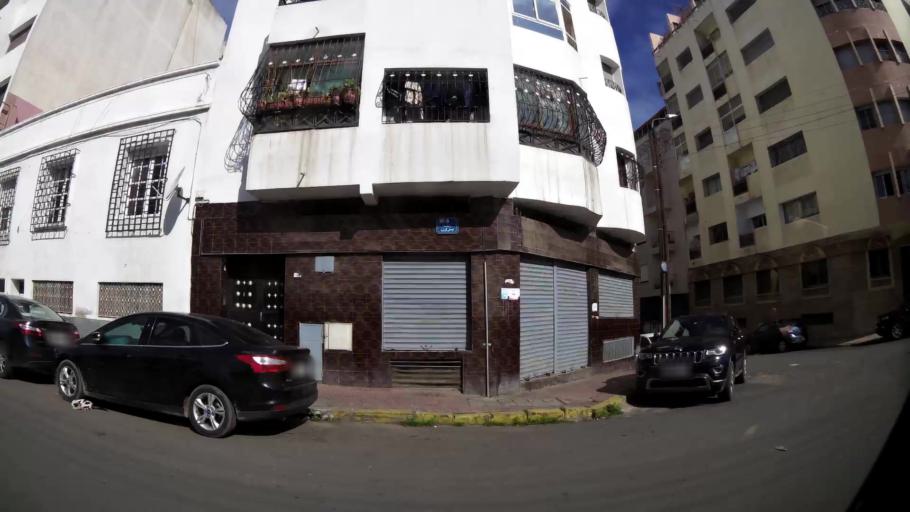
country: MA
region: Grand Casablanca
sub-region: Casablanca
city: Casablanca
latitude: 33.5949
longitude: -7.5925
